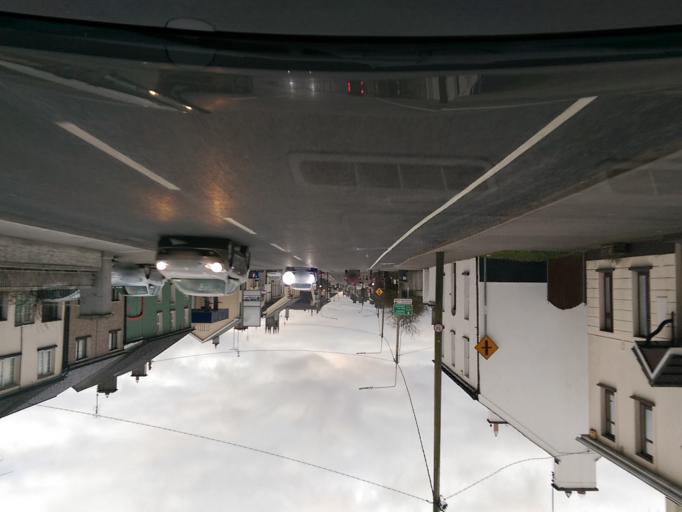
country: IE
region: Leinster
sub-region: Uibh Fhaili
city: Birr
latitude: 53.1014
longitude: -7.9079
